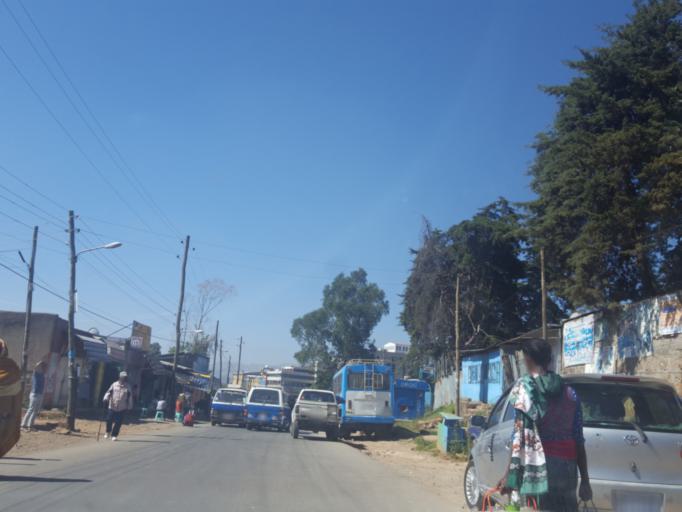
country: ET
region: Adis Abeba
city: Addis Ababa
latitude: 9.0607
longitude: 38.7401
